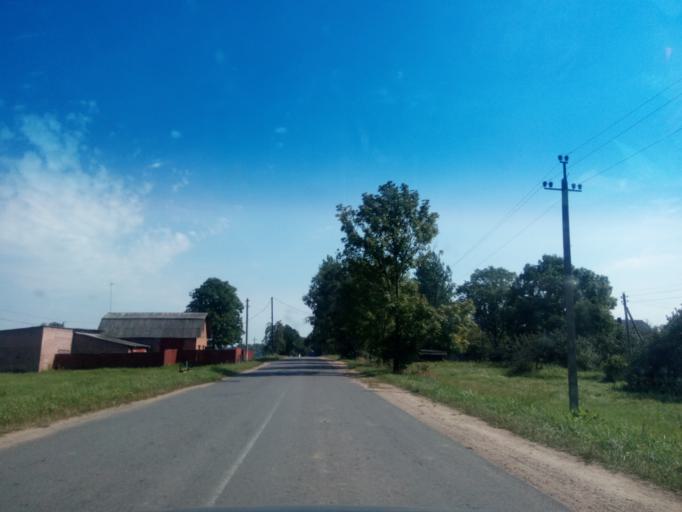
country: BY
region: Vitebsk
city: Vyerkhnyadzvinsk
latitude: 55.8354
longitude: 27.7310
